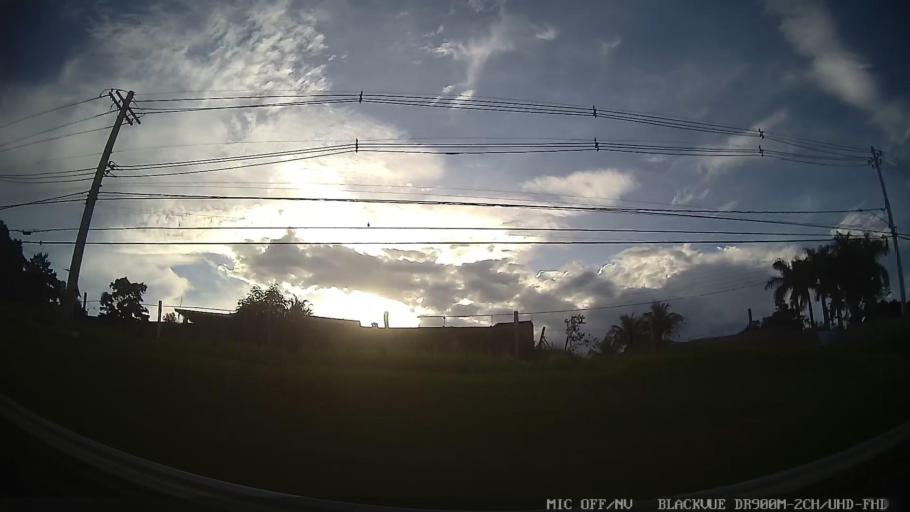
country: BR
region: Sao Paulo
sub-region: Tiete
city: Tiete
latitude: -23.0678
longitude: -47.7295
